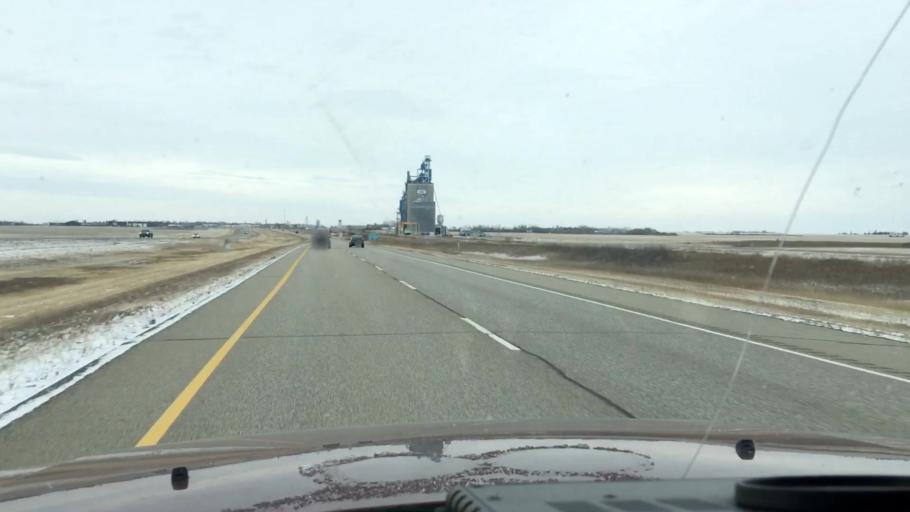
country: CA
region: Saskatchewan
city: Watrous
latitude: 51.2849
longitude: -106.0218
